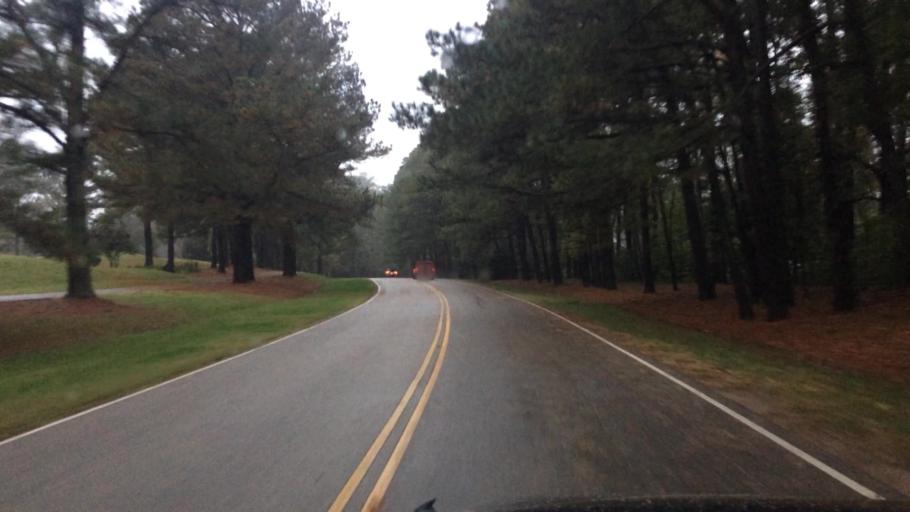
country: US
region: Virginia
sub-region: City of Williamsburg
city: Williamsburg
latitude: 37.2329
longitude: -76.6763
